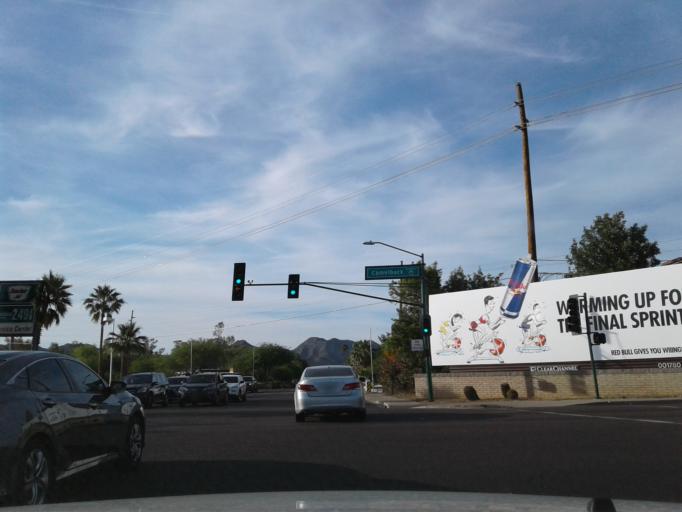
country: US
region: Arizona
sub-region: Maricopa County
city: Paradise Valley
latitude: 33.5097
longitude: -111.9953
